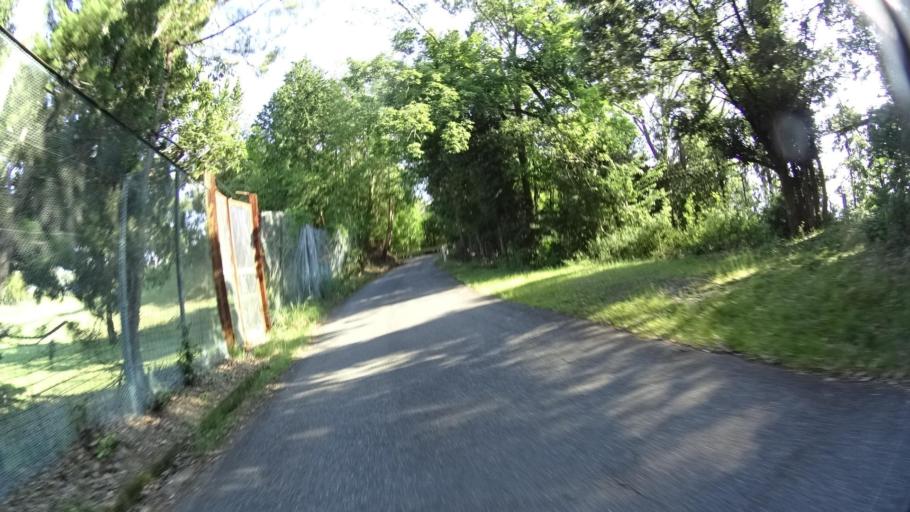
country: JP
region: Kyoto
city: Kameoka
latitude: 34.9838
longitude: 135.5563
